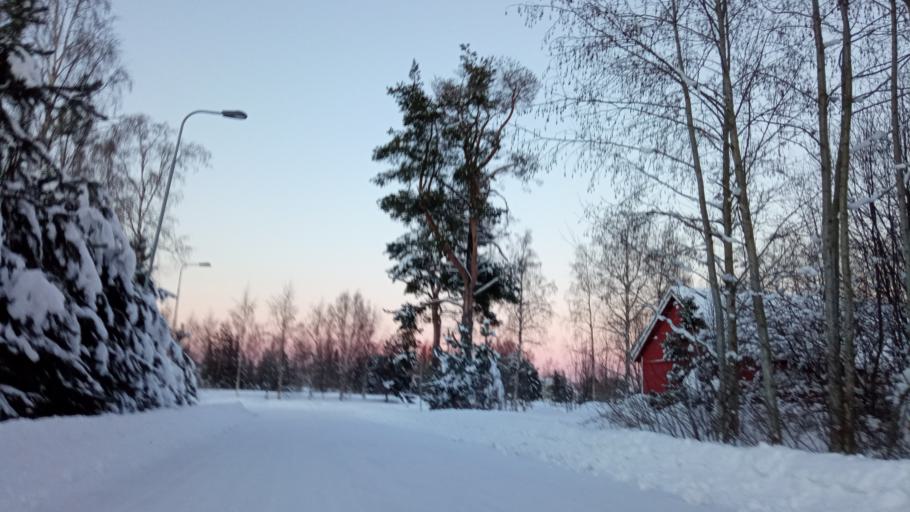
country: FI
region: Southern Ostrobothnia
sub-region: Jaerviseutu
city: Alajaervi
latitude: 62.9901
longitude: 23.8539
